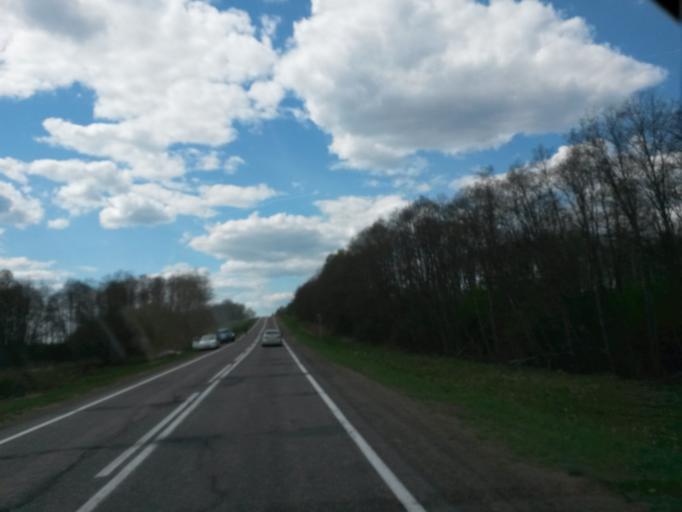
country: RU
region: Jaroslavl
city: Bol'shoye Selo
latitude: 57.7261
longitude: 39.0324
